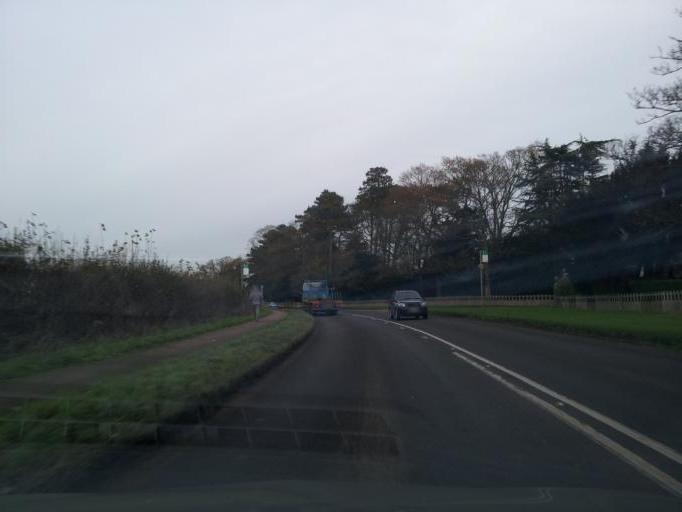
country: GB
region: England
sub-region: Central Bedfordshire
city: Leighton Buzzard
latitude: 51.8984
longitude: -0.7073
